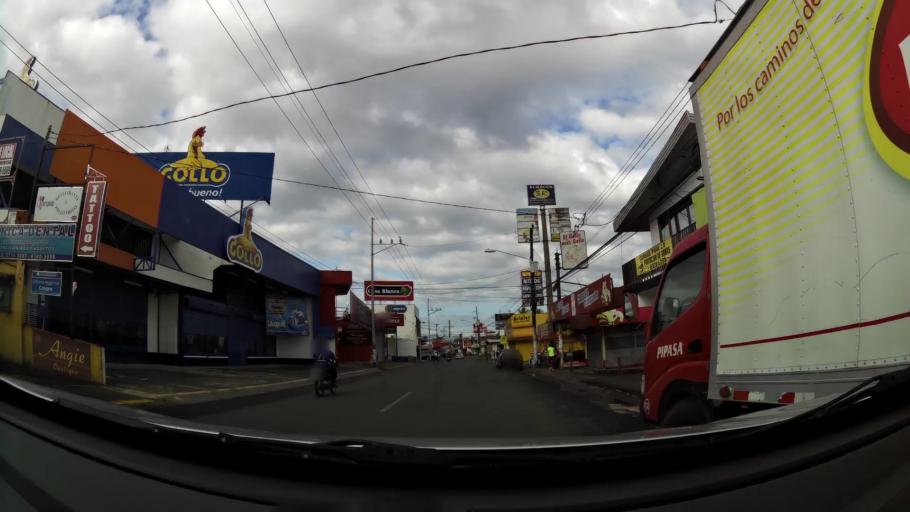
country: CR
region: Limon
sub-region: Canton de Pococi
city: Guapiles
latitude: 10.2156
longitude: -83.7851
